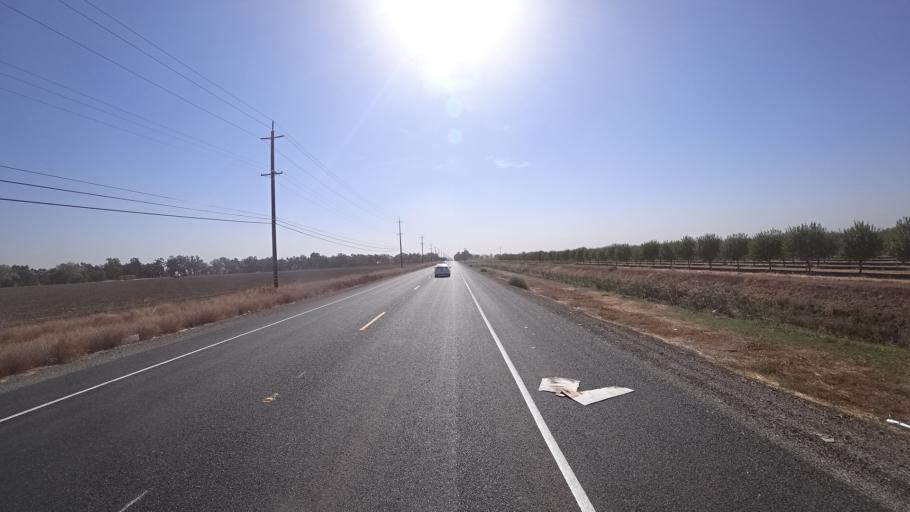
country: US
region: California
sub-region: Yolo County
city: Woodland
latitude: 38.6354
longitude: -121.7290
